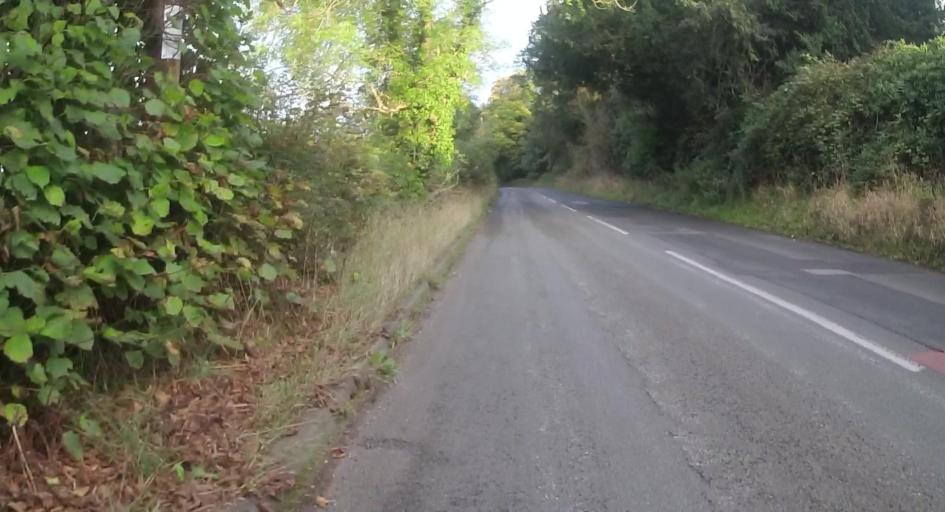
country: GB
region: England
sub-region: Hampshire
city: Tadley
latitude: 51.3814
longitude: -1.1438
